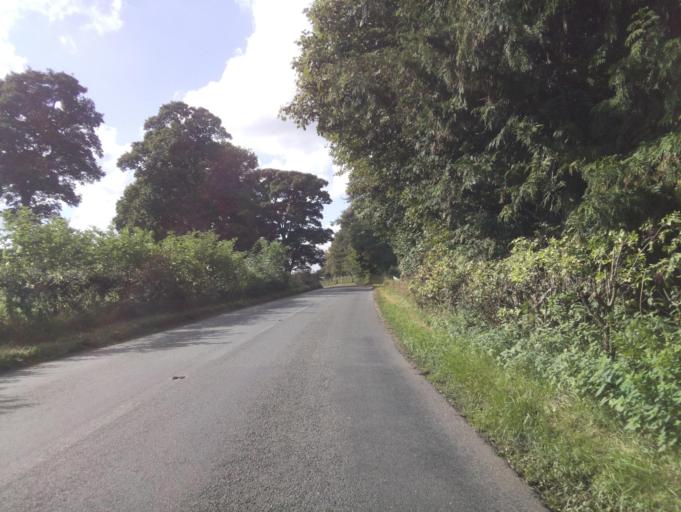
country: GB
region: England
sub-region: North Yorkshire
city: Leyburn
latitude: 54.2672
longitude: -1.7505
